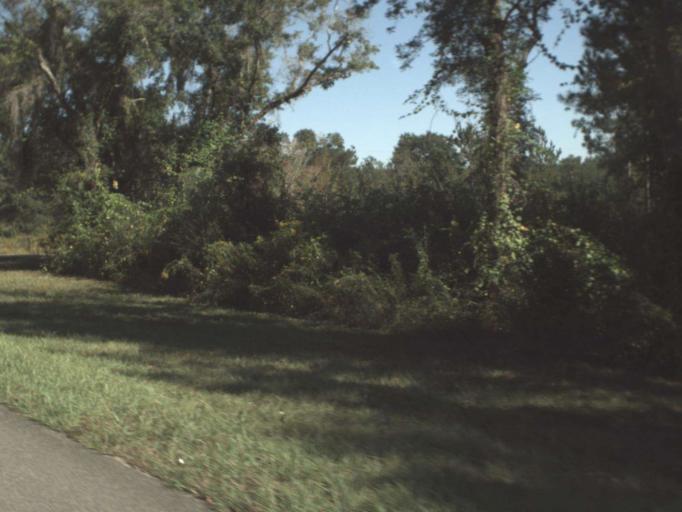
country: US
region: Florida
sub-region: Walton County
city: DeFuniak Springs
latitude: 30.6171
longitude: -85.9434
